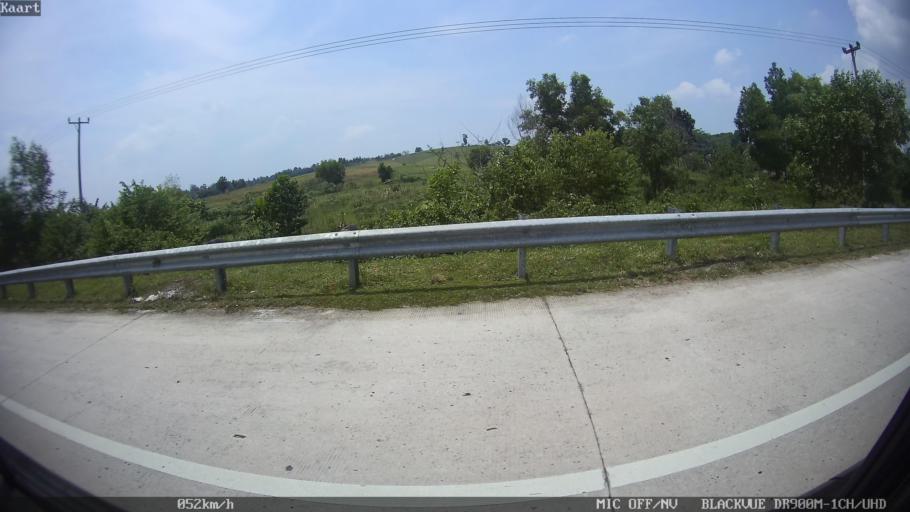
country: ID
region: Lampung
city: Natar
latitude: -5.2811
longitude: 105.2064
